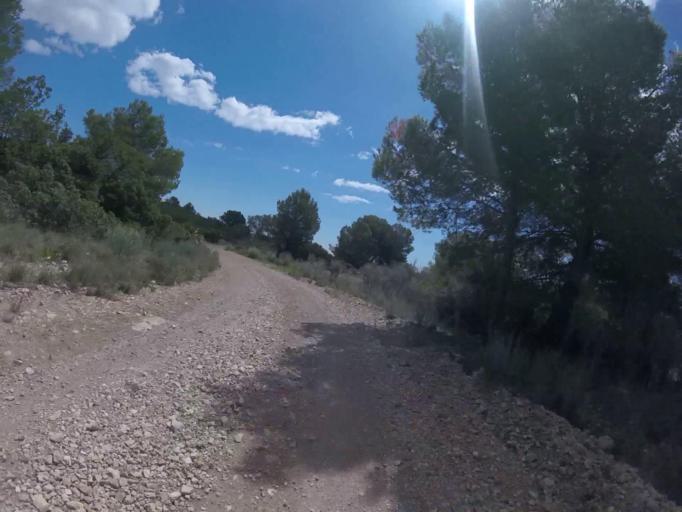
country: ES
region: Valencia
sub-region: Provincia de Castello
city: Alcoceber
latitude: 40.2847
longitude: 0.3236
